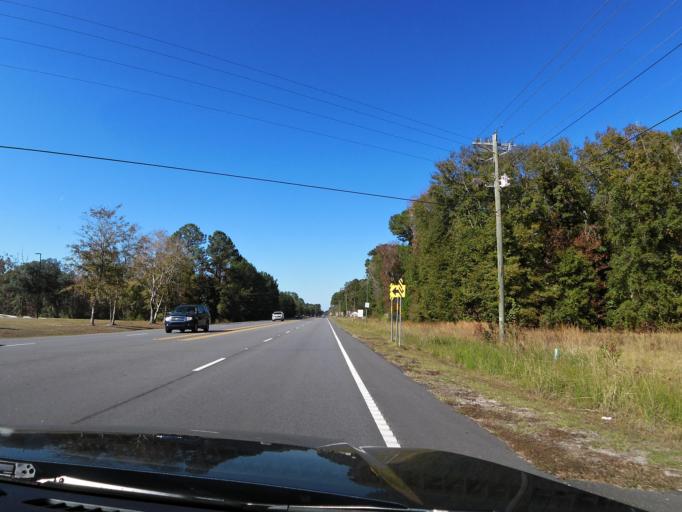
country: US
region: Georgia
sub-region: Liberty County
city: Midway
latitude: 31.7880
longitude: -81.3943
